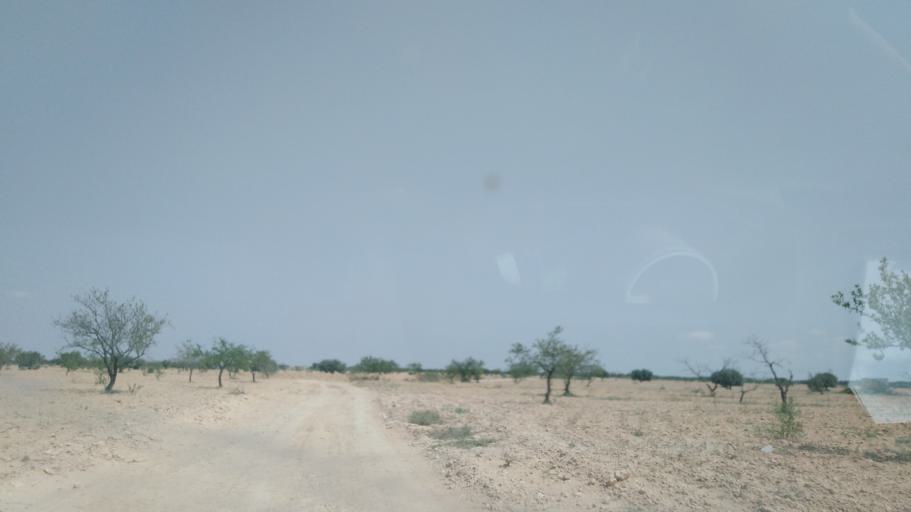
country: TN
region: Safaqis
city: Sfax
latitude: 34.6460
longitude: 10.5583
